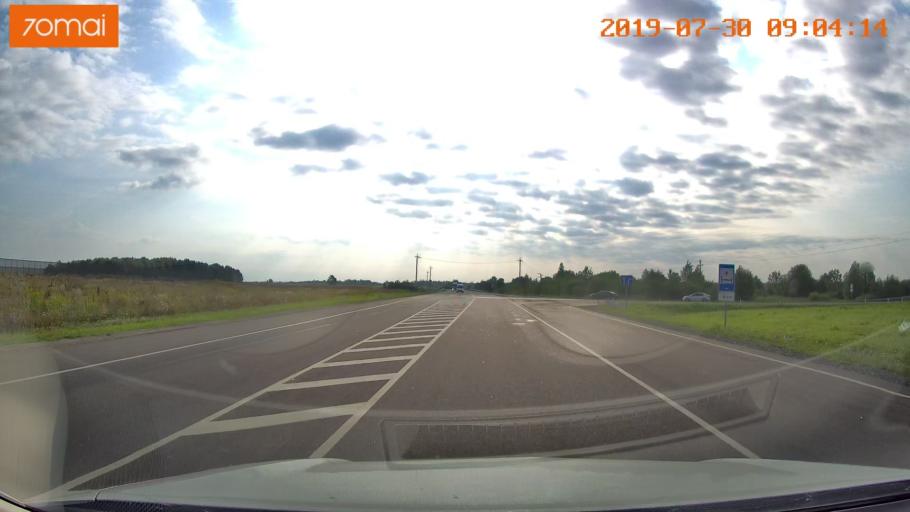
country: RU
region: Kaliningrad
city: Gusev
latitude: 54.6050
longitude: 22.2750
